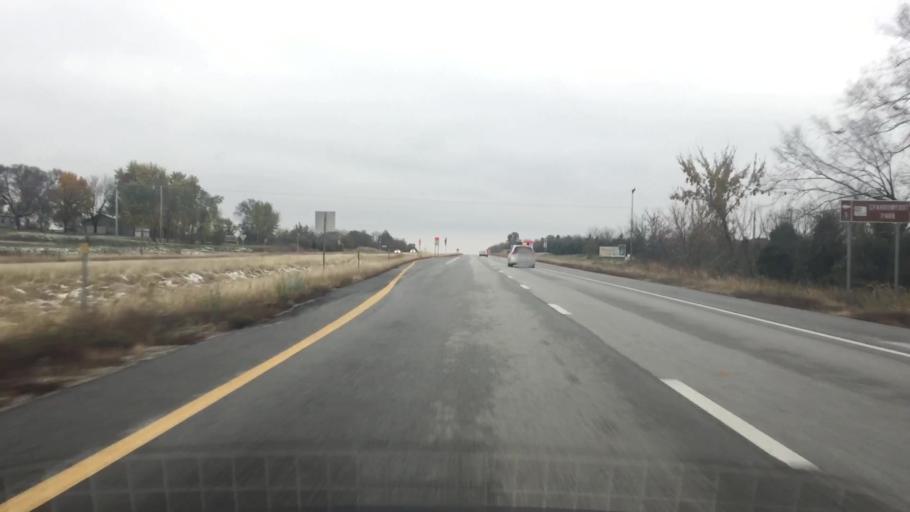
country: US
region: Missouri
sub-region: Henry County
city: Clinton
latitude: 38.3025
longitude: -93.7588
